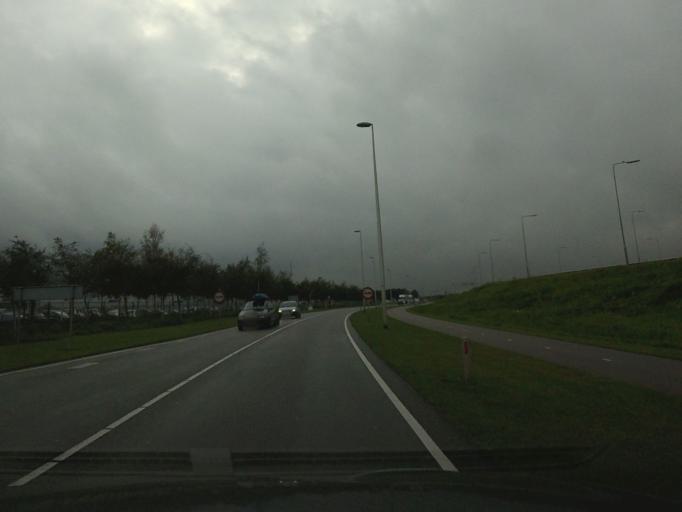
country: NL
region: North Holland
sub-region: Gemeente Aalsmeer
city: Aalsmeer
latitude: 52.2901
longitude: 4.7322
